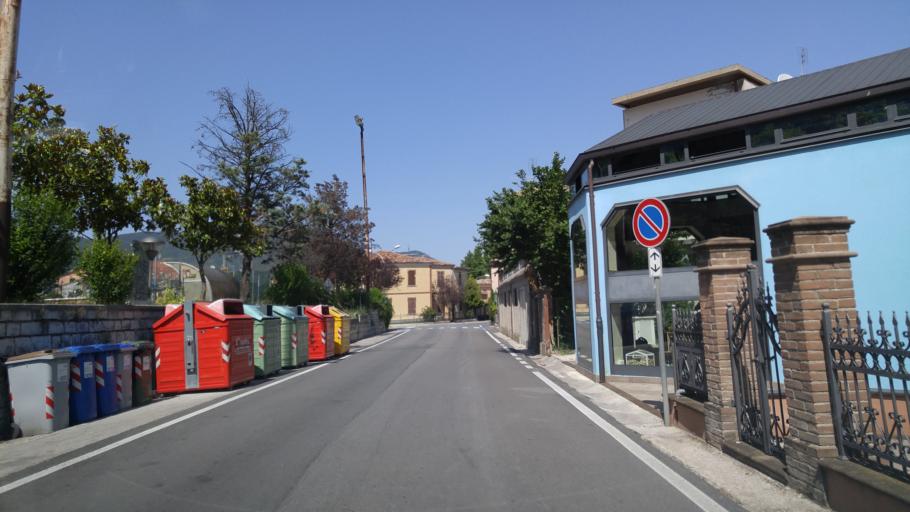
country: IT
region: The Marches
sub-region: Provincia di Pesaro e Urbino
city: Acqualagna
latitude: 43.6171
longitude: 12.6706
